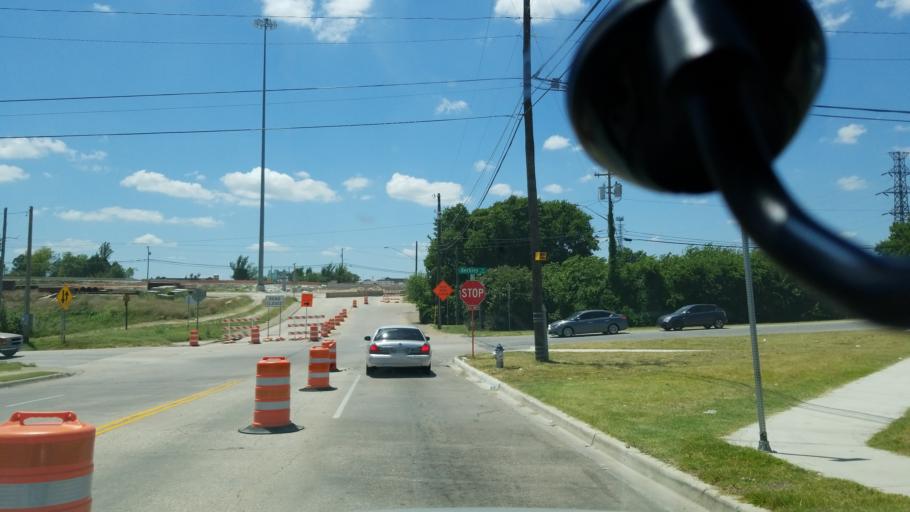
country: US
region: Texas
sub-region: Dallas County
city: Cockrell Hill
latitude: 32.7010
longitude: -96.8226
